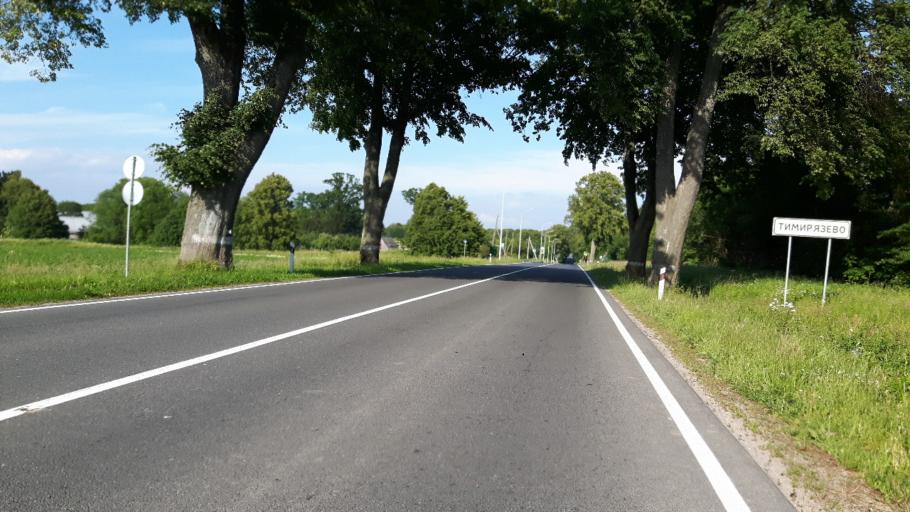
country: RU
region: Kaliningrad
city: Mamonovo
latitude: 54.4889
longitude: 20.0468
